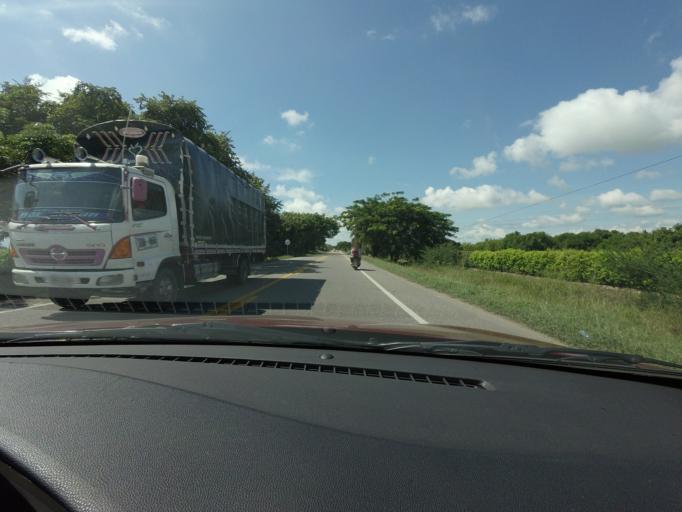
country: CO
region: Tolima
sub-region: Flandes
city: Flandes
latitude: 4.2284
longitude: -74.8422
